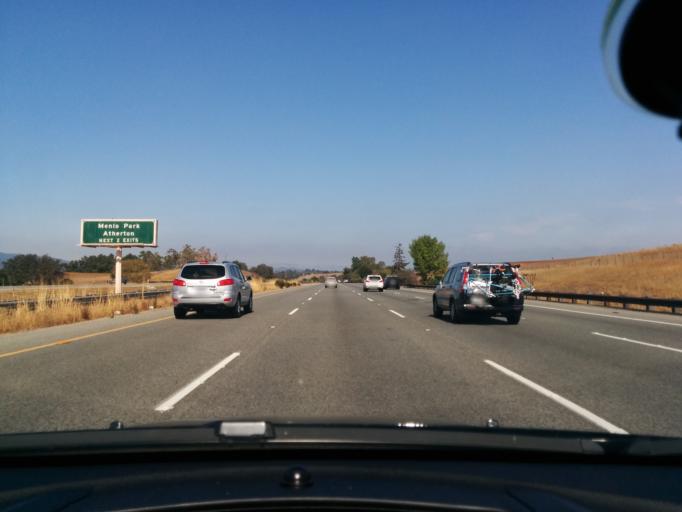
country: US
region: California
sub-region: San Mateo County
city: Ladera
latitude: 37.4022
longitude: -122.1844
